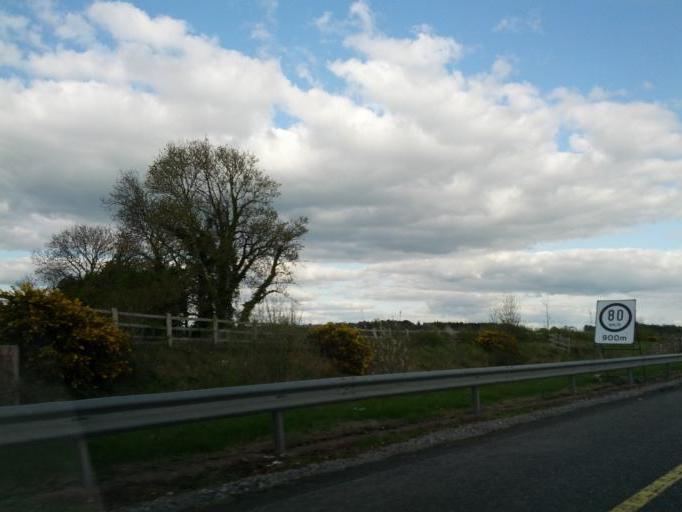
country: IE
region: Leinster
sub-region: An Iarmhi
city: Athlone
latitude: 53.4038
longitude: -7.8740
